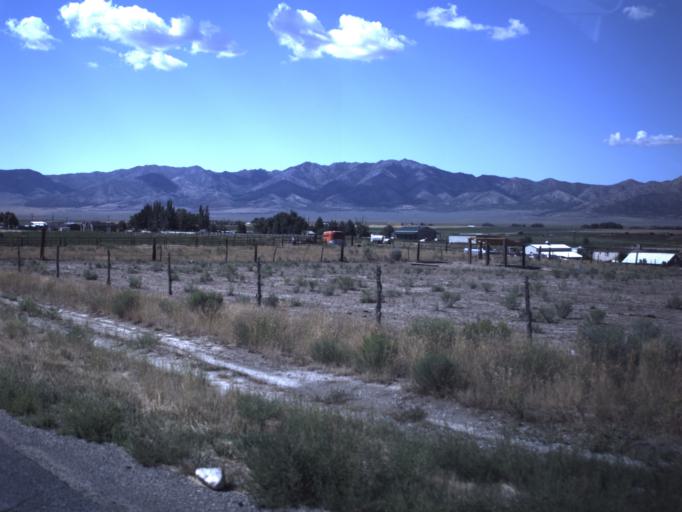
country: US
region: Utah
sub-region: Tooele County
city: Tooele
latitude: 40.0920
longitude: -112.4309
